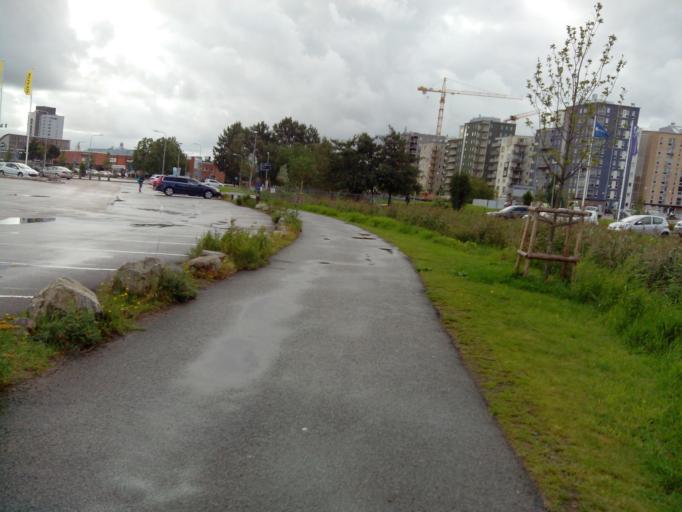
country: SE
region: Vaestra Goetaland
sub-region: Goteborg
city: Goeteborg
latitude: 57.7251
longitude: 11.9510
